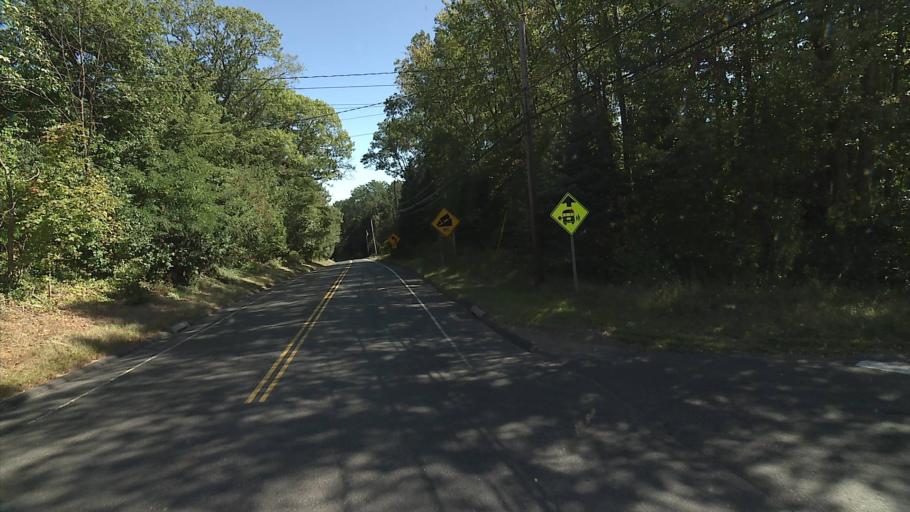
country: US
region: Connecticut
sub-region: New Haven County
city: Prospect
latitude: 41.4987
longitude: -72.9557
